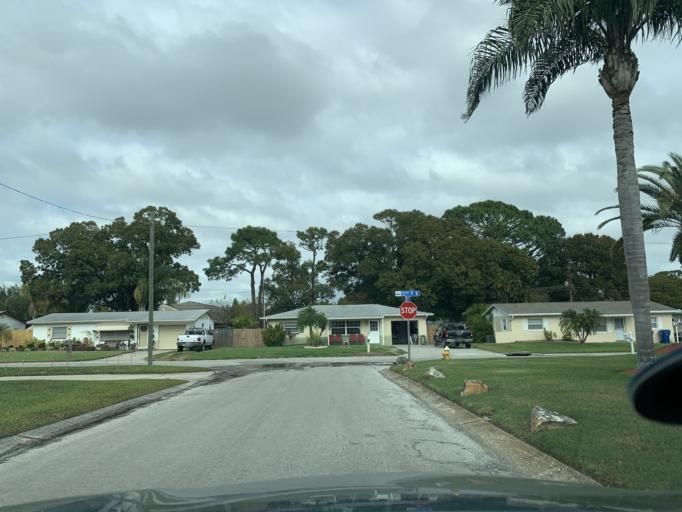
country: US
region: Florida
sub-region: Pinellas County
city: Largo
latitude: 27.8886
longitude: -82.7831
